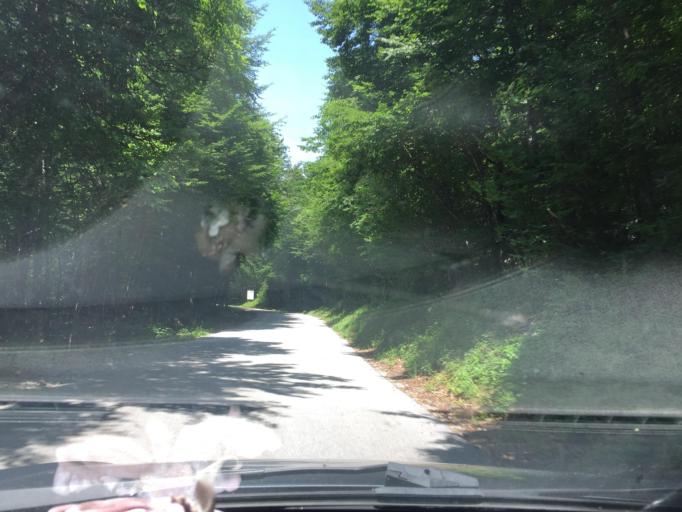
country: HR
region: Istarska
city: Buzet
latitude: 45.4688
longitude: 14.1130
